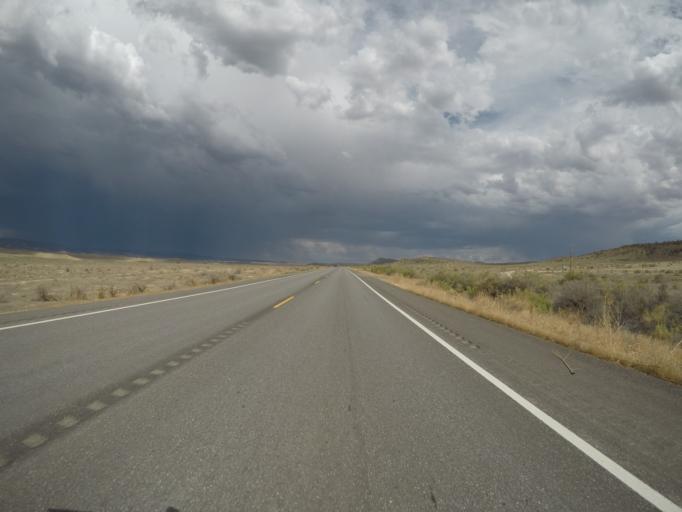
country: US
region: Utah
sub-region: Uintah County
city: Naples
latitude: 40.2968
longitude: -109.1844
